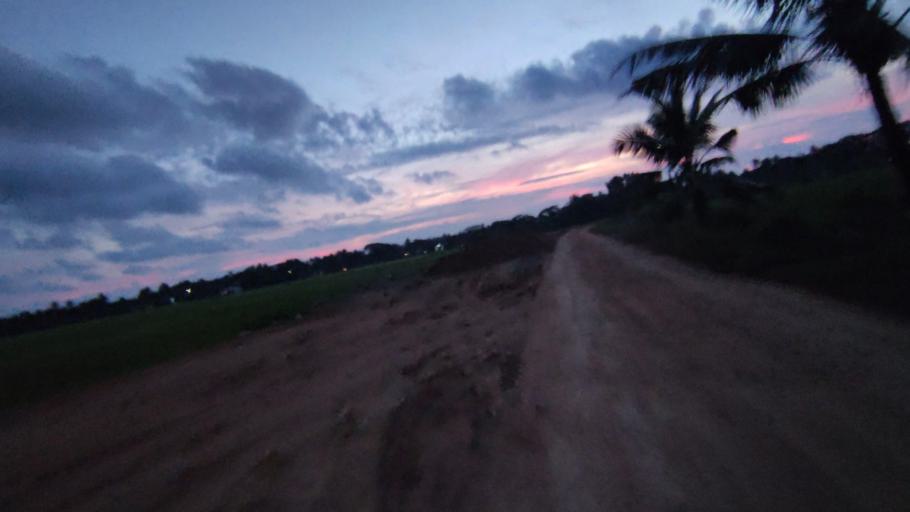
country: IN
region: Kerala
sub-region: Alappuzha
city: Shertallai
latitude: 9.6418
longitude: 76.4329
